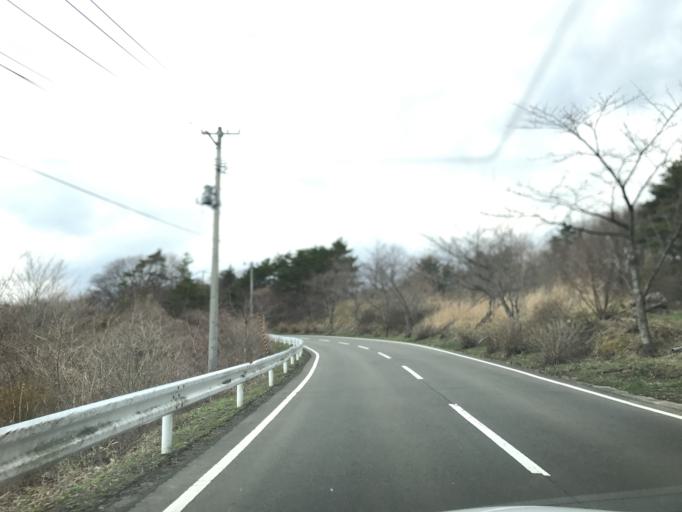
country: JP
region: Miyagi
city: Shiroishi
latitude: 38.0312
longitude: 140.5408
